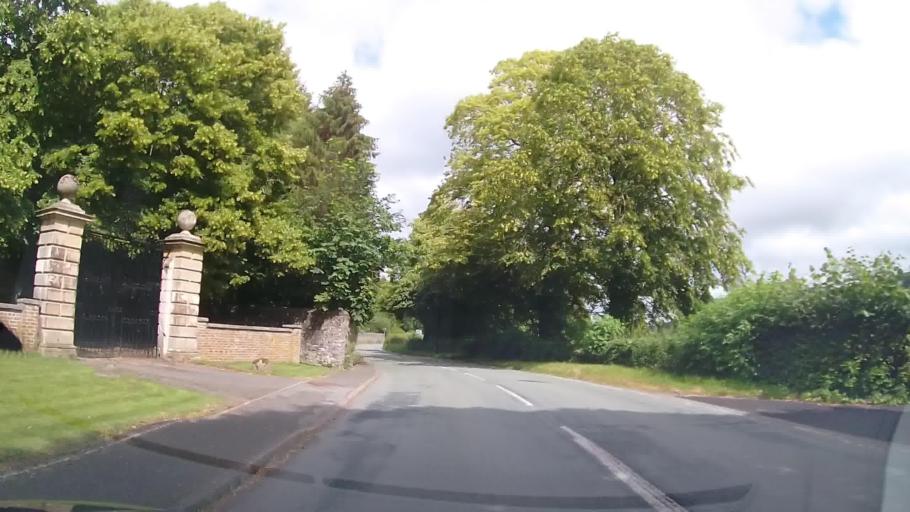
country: GB
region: Wales
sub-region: Sir Powys
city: Llanfechain
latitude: 52.8095
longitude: -3.2054
